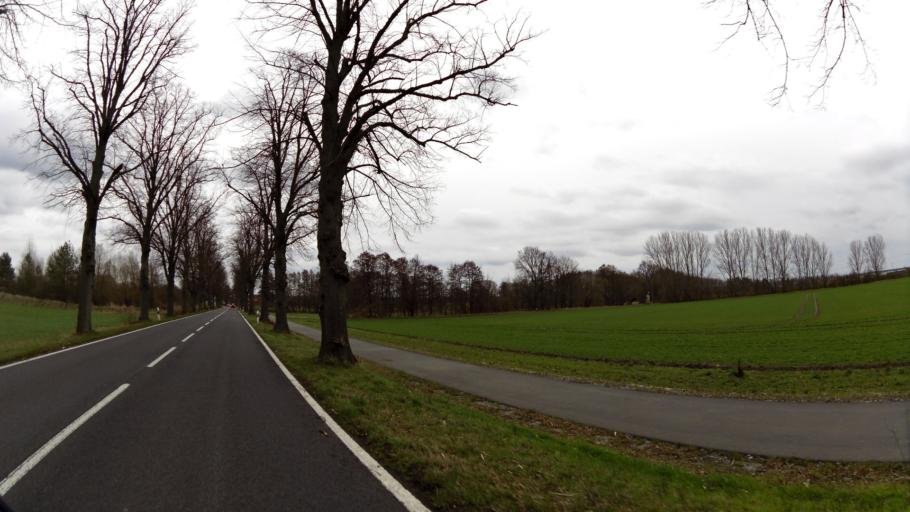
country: DE
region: Brandenburg
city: Schonefeld
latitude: 52.3468
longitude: 13.5422
